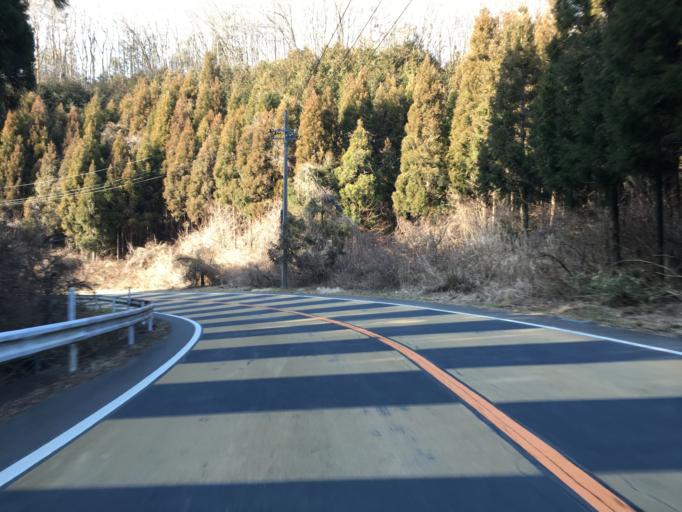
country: JP
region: Ibaraki
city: Takahagi
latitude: 36.7372
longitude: 140.5542
